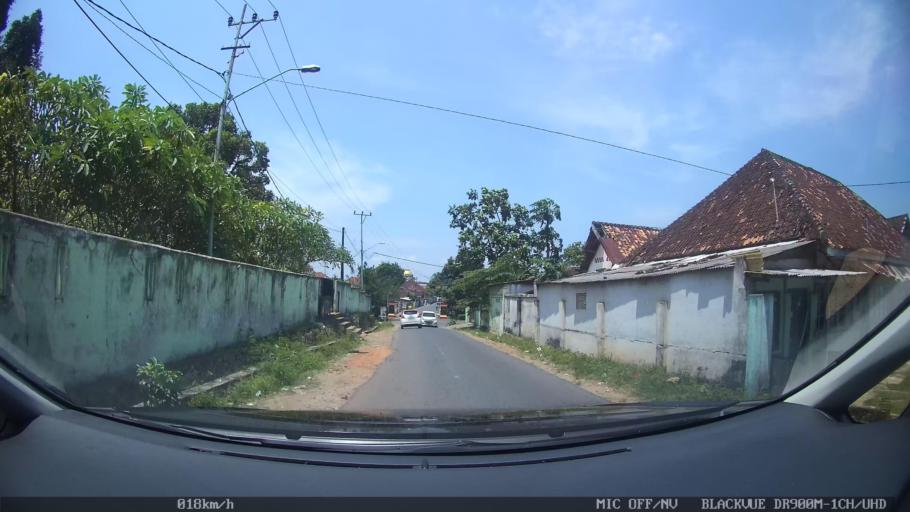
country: ID
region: Lampung
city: Kedaton
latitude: -5.4035
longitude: 105.2626
